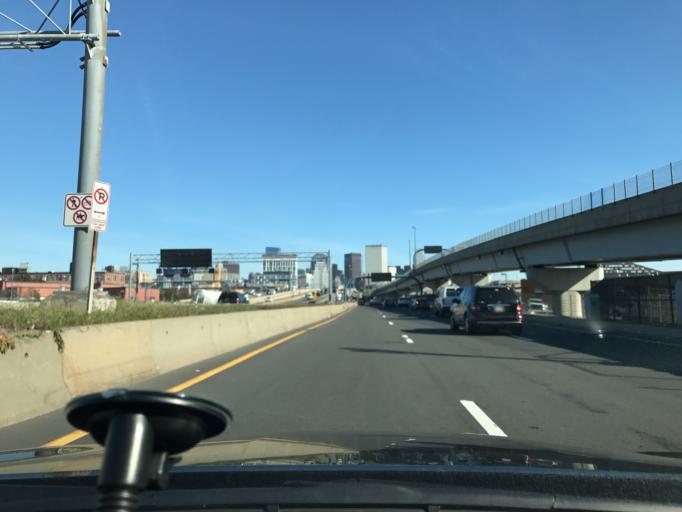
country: US
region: Massachusetts
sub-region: Suffolk County
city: South Boston
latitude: 42.3369
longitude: -71.0645
